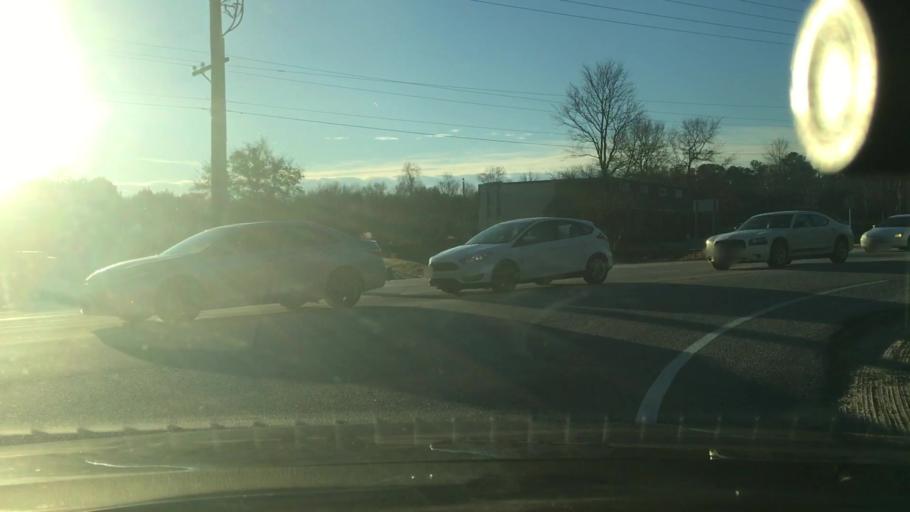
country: US
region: Georgia
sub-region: Fayette County
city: Peachtree City
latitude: 33.3413
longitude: -84.6459
